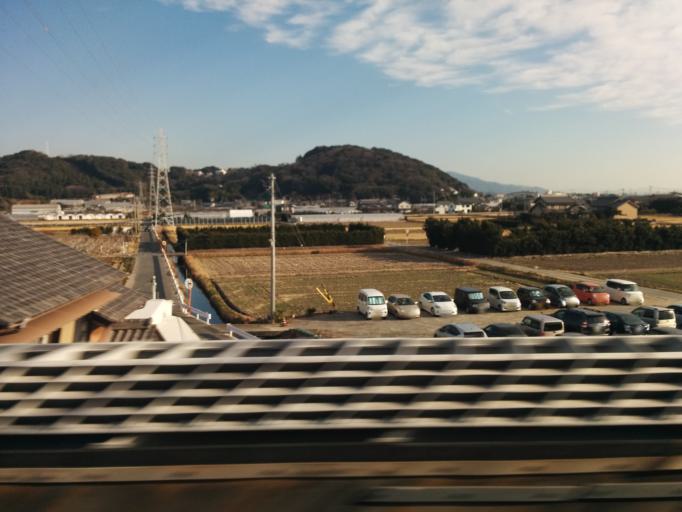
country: JP
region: Aichi
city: Kozakai-cho
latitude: 34.8109
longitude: 137.3041
